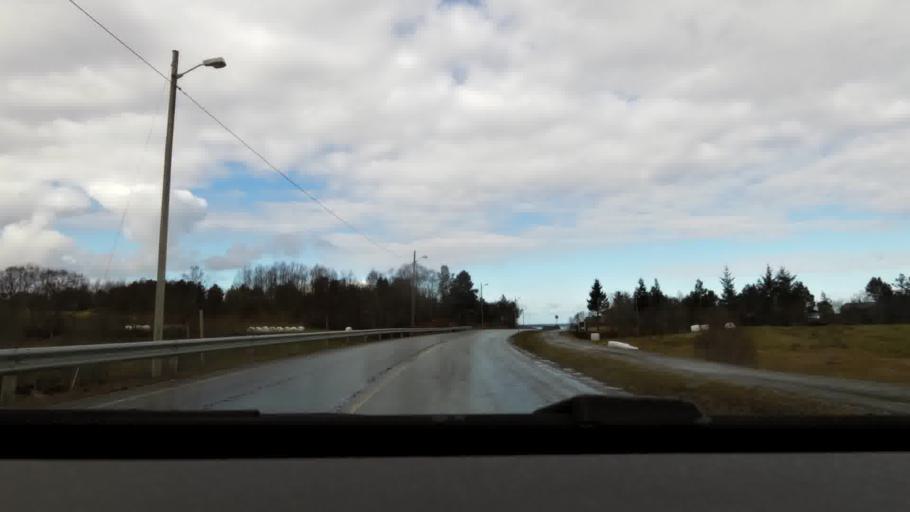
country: NO
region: More og Romsdal
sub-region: Eide
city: Eide
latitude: 62.9641
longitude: 7.3575
